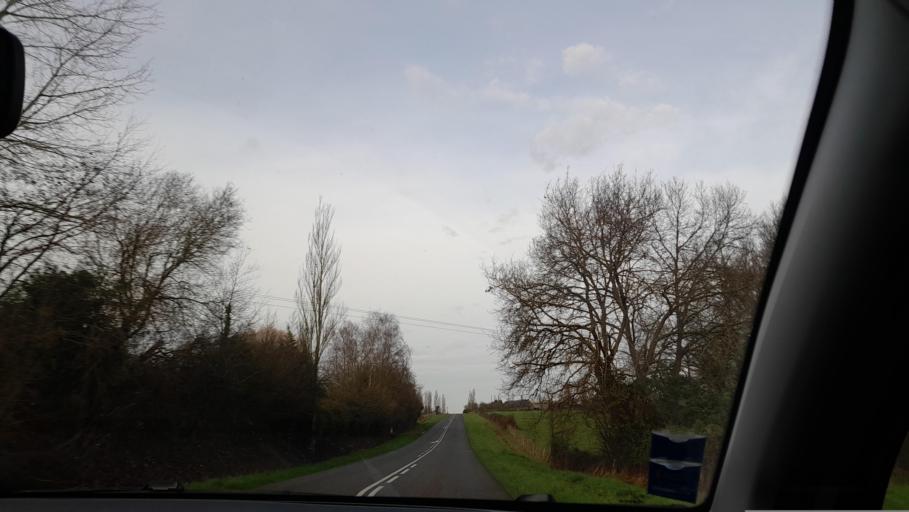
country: FR
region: Pays de la Loire
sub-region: Departement de la Mayenne
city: Craon
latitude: 47.8567
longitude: -0.9704
